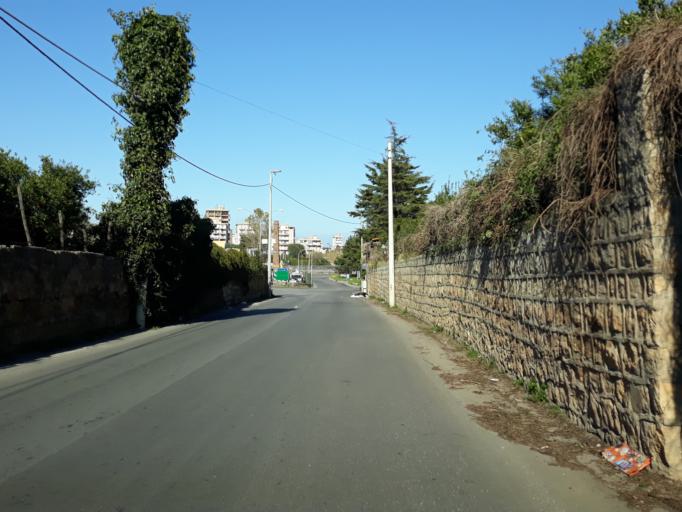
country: IT
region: Sicily
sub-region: Palermo
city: Ciaculli
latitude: 38.0877
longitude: 13.3826
